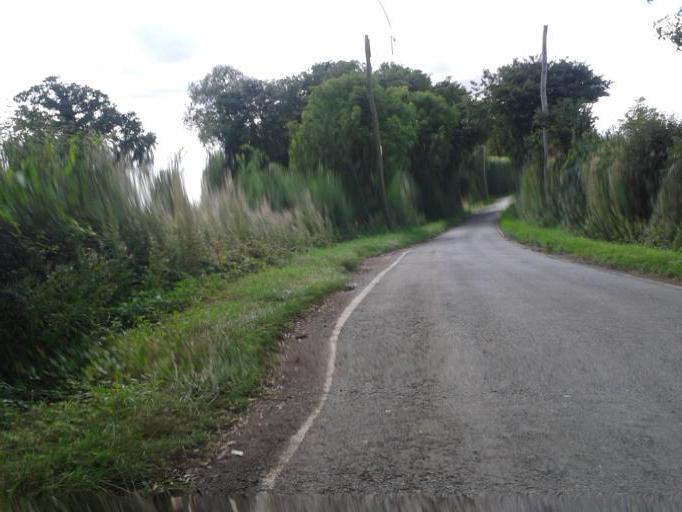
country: GB
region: England
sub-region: Cambridgeshire
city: Duxford
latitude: 51.9957
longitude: 0.1010
